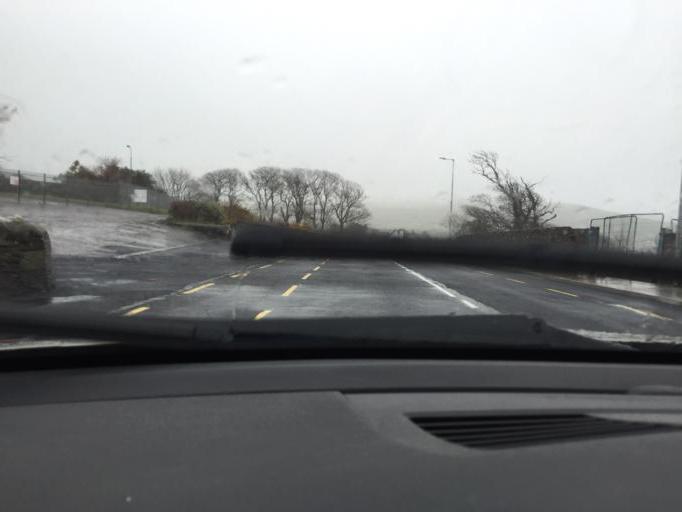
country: IE
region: Munster
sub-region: Ciarrai
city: Dingle
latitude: 52.1443
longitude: -10.2773
